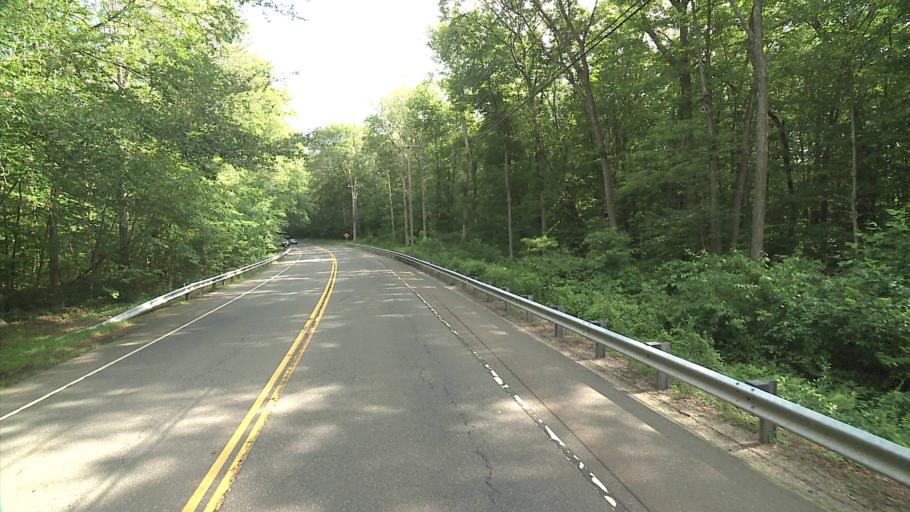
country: US
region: Connecticut
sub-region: Middlesex County
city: Clinton
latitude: 41.3285
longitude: -72.4914
